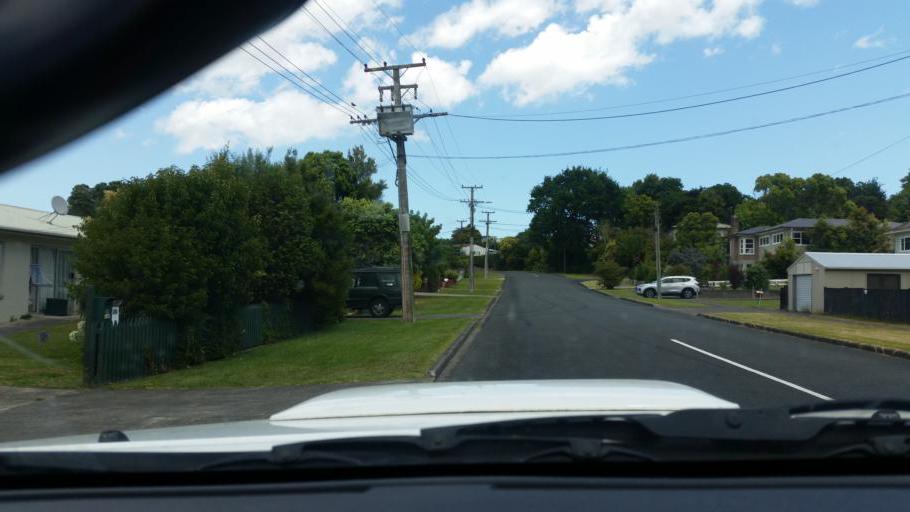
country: NZ
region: Northland
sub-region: Kaipara District
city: Dargaville
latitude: -35.9366
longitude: 173.8665
